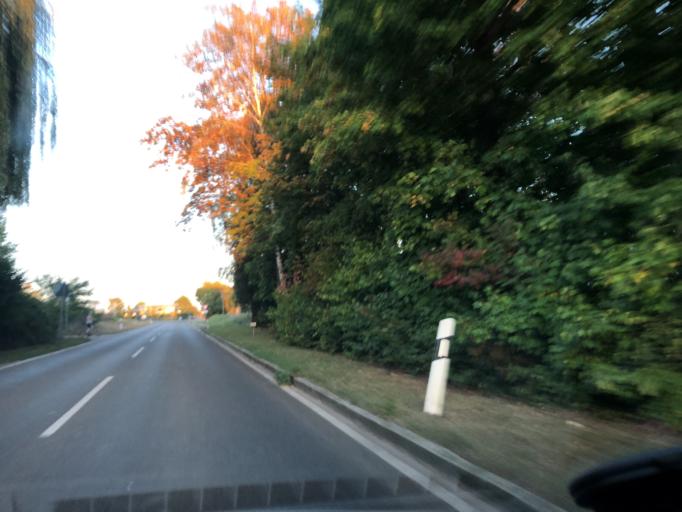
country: DE
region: Baden-Wuerttemberg
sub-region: Regierungsbezirk Stuttgart
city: Marbach am Neckar
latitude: 48.9145
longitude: 9.2624
